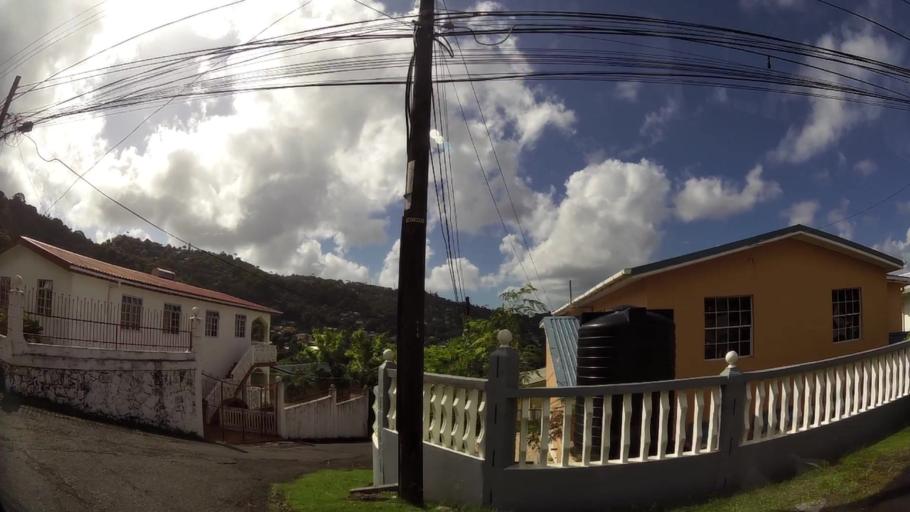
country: LC
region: Castries Quarter
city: Bisee
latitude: 14.0009
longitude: -60.9801
